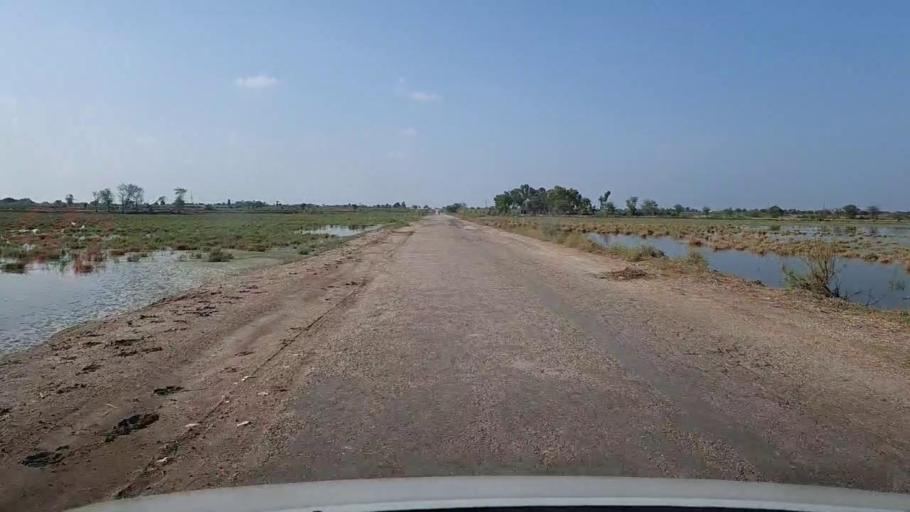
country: PK
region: Sindh
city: Kandiaro
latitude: 27.0619
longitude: 68.3160
